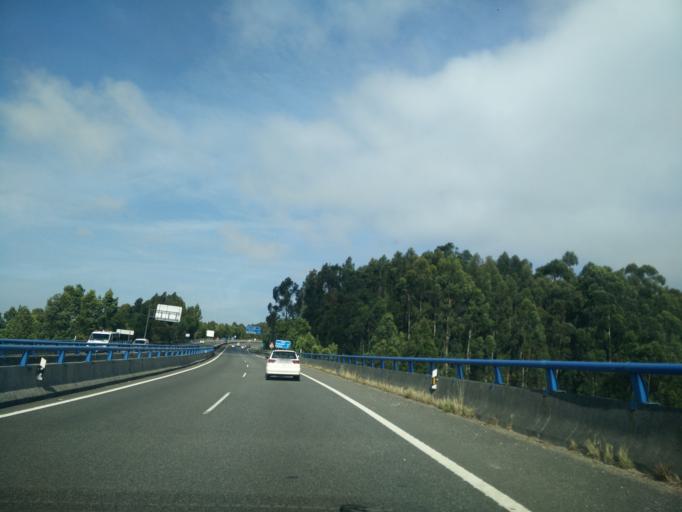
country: ES
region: Galicia
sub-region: Provincia de Pontevedra
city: Vigo
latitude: 42.1953
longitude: -8.7599
